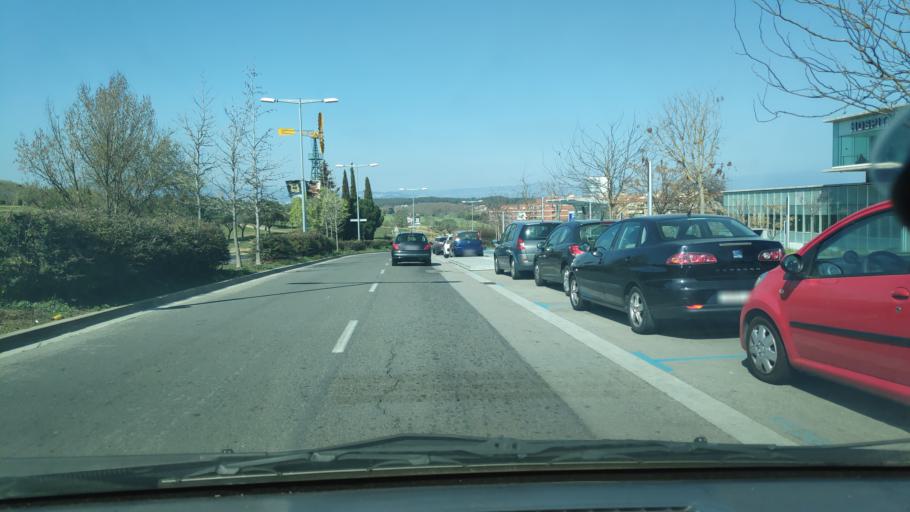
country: ES
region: Catalonia
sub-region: Provincia de Barcelona
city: Mollet del Valles
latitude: 41.5434
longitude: 2.2015
